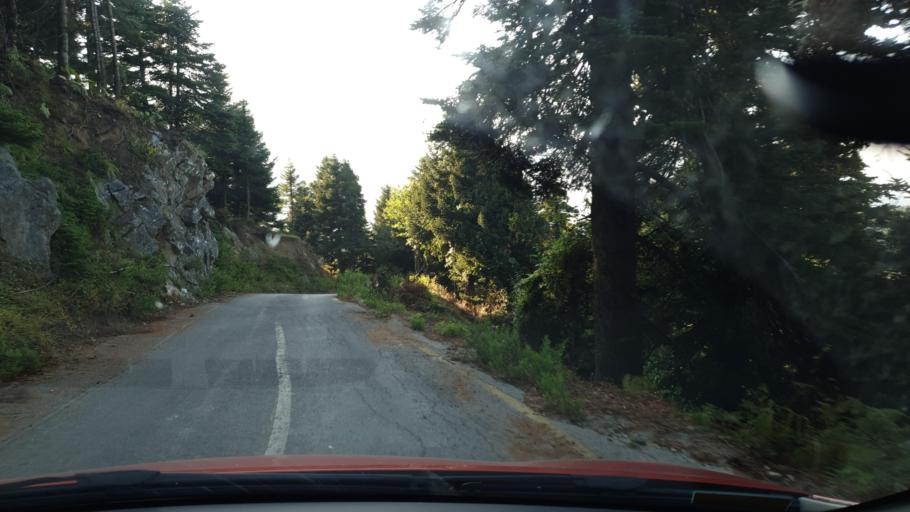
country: GR
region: Central Greece
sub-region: Nomos Evvoias
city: Yimnon
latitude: 38.5990
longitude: 23.9014
